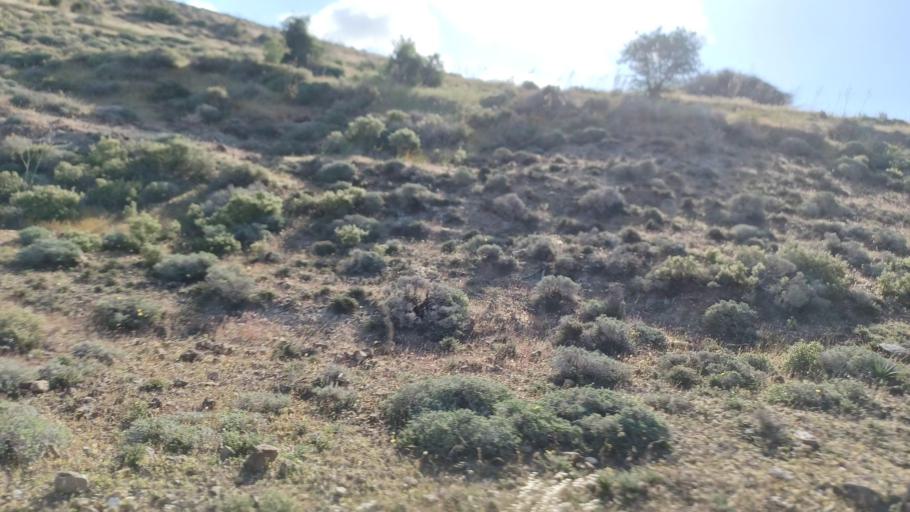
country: CY
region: Lefkosia
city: Peristerona
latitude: 35.0684
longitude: 33.0548
